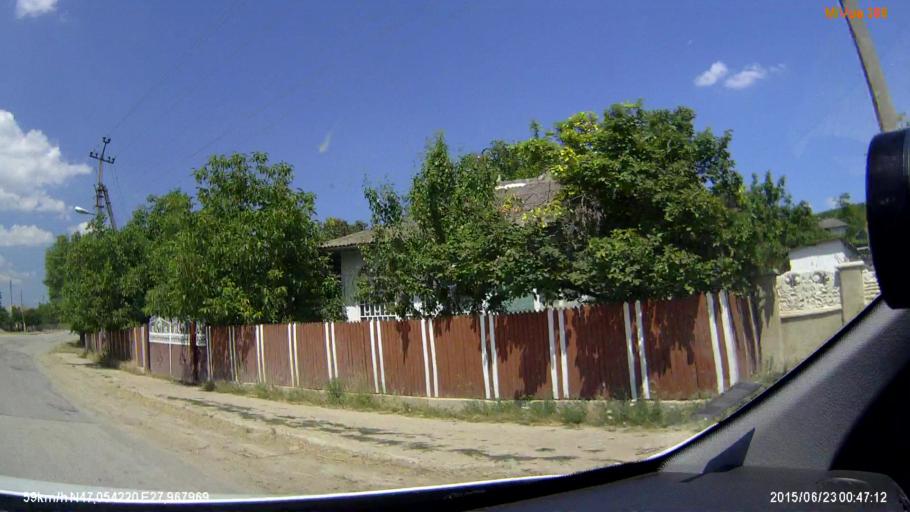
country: RO
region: Iasi
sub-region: Comuna Costuleni
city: Cozia
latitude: 47.0541
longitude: 27.9681
